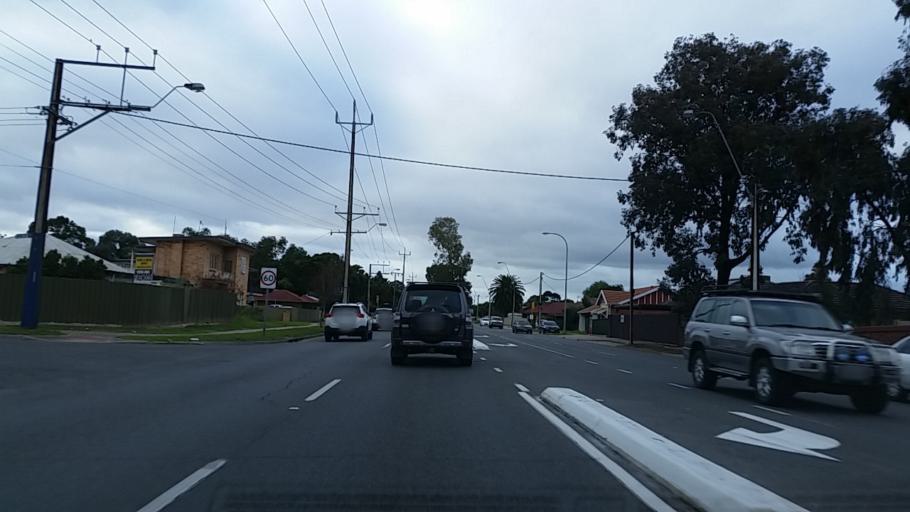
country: AU
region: South Australia
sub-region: Salisbury
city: Salisbury
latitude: -34.7701
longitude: 138.6345
